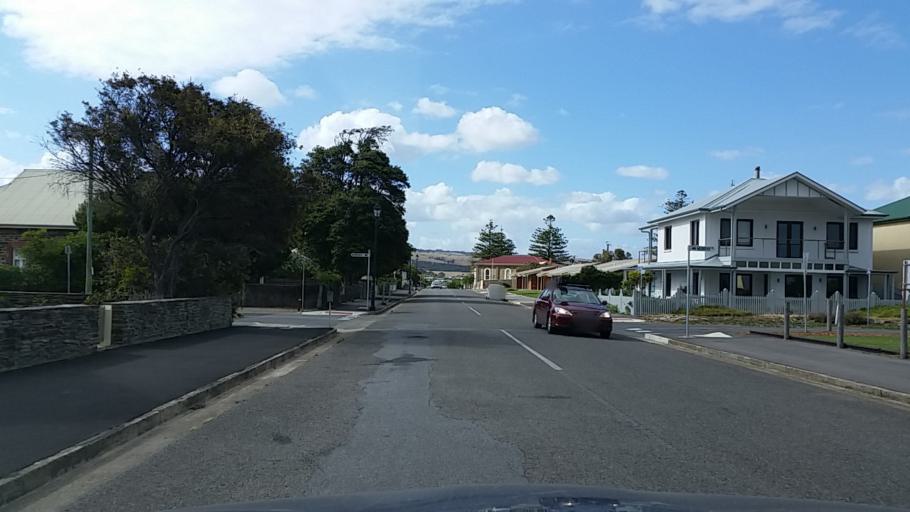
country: AU
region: South Australia
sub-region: Alexandrina
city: Port Elliot
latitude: -35.5348
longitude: 138.6821
